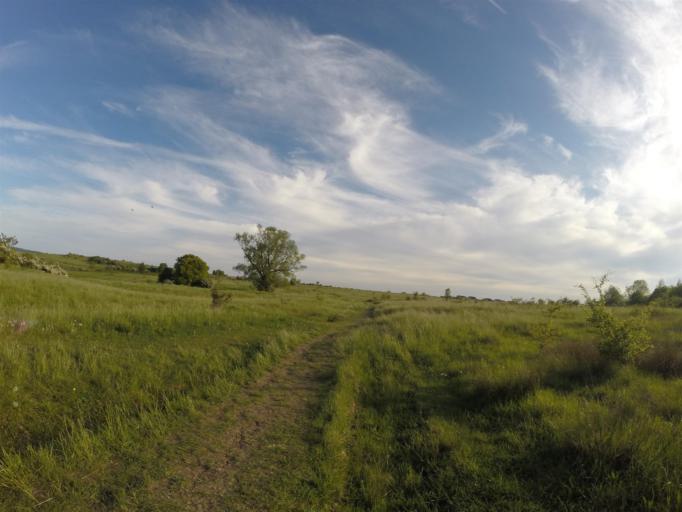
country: DE
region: Thuringia
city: Lehesten
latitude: 50.9553
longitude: 11.5699
